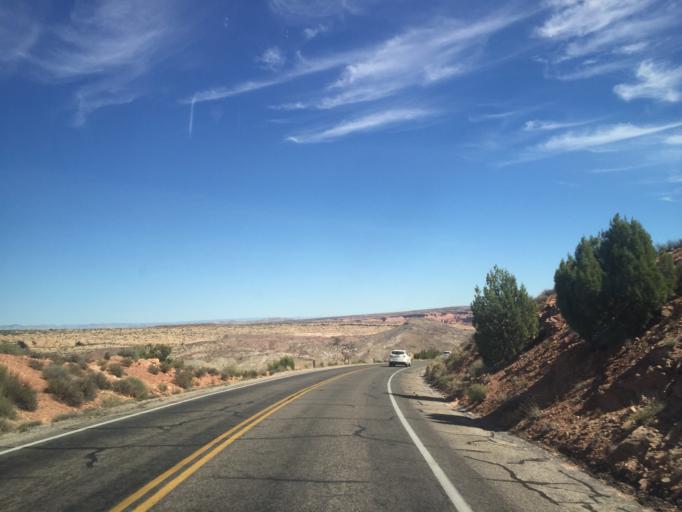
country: US
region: Utah
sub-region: Grand County
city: Moab
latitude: 38.7195
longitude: -109.5556
